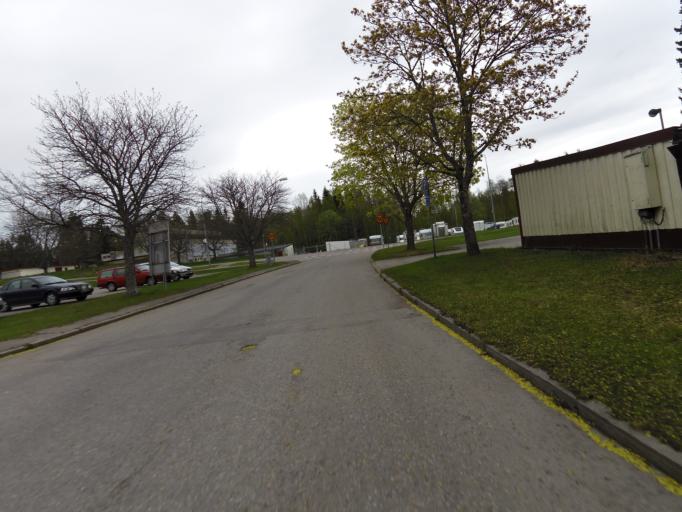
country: SE
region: Gaevleborg
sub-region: Gavle Kommun
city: Gavle
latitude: 60.6916
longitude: 17.1227
